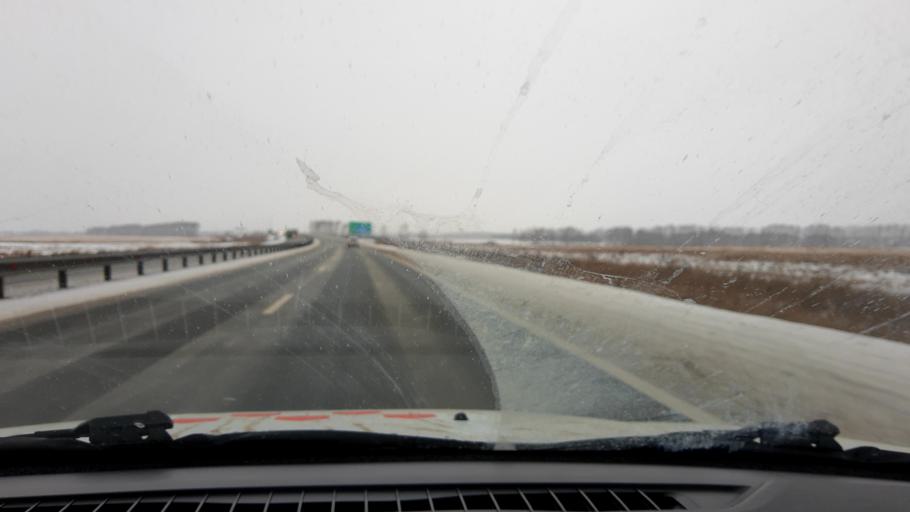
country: RU
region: Nizjnij Novgorod
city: Burevestnik
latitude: 56.1188
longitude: 43.9419
